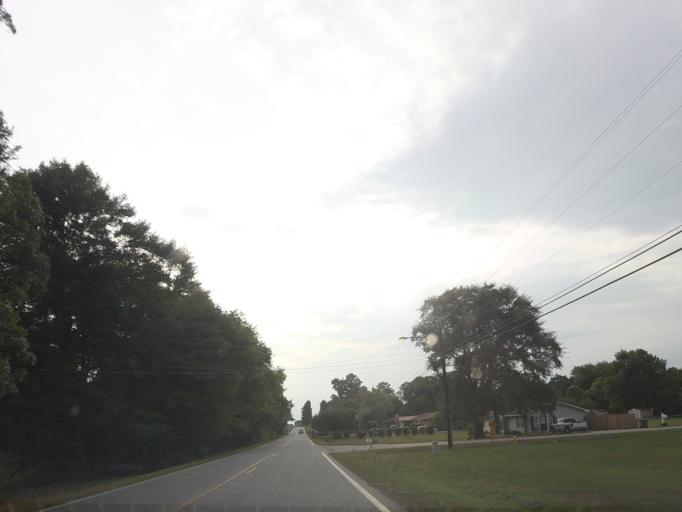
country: US
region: Georgia
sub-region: Houston County
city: Centerville
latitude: 32.7170
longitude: -83.6993
